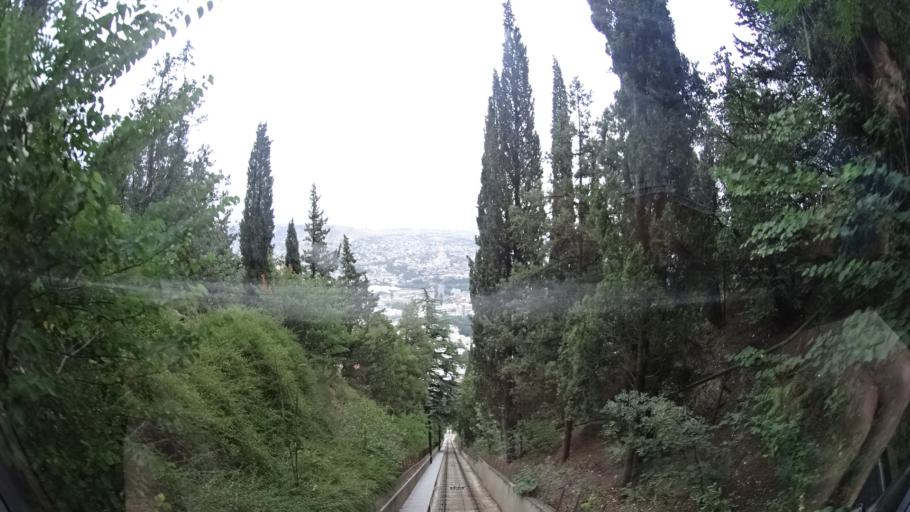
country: GE
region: T'bilisi
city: Tbilisi
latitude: 41.6950
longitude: 44.7873
